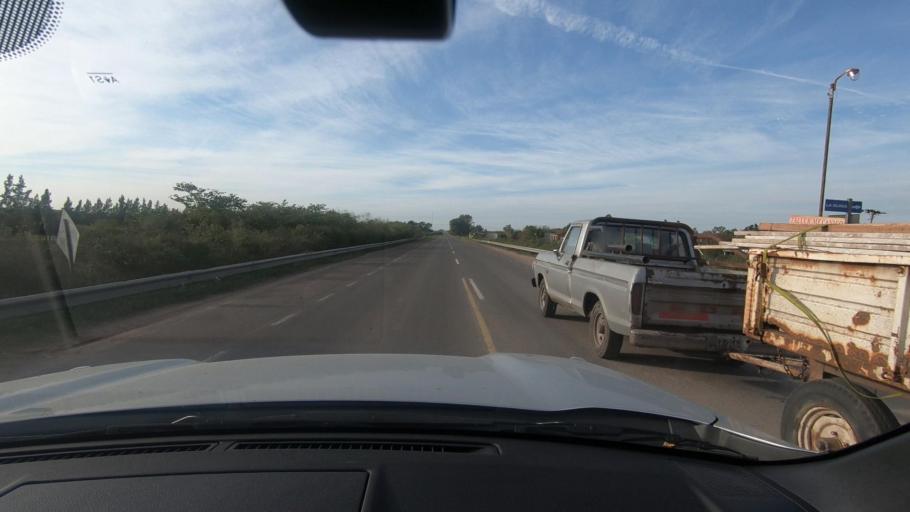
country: AR
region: Entre Rios
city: Colon
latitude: -32.2554
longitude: -58.2183
